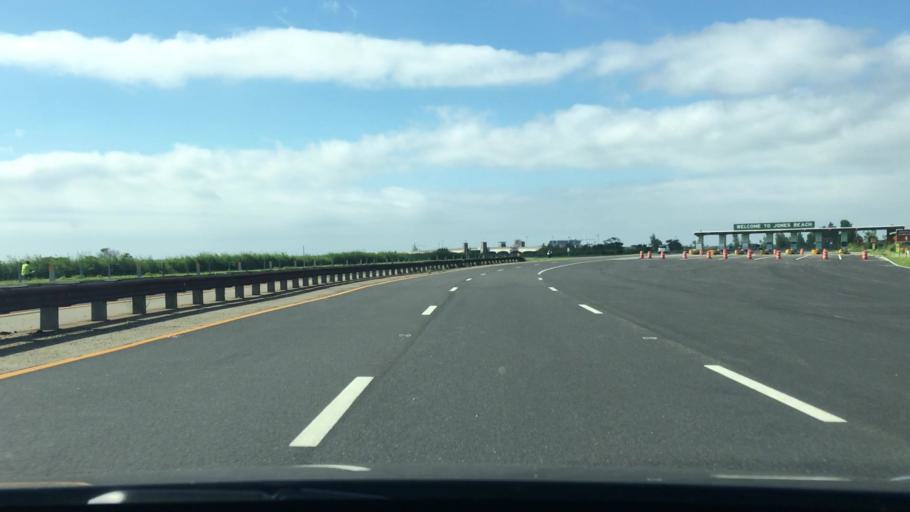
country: US
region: New York
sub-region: Nassau County
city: Seaford
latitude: 40.6213
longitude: -73.5008
